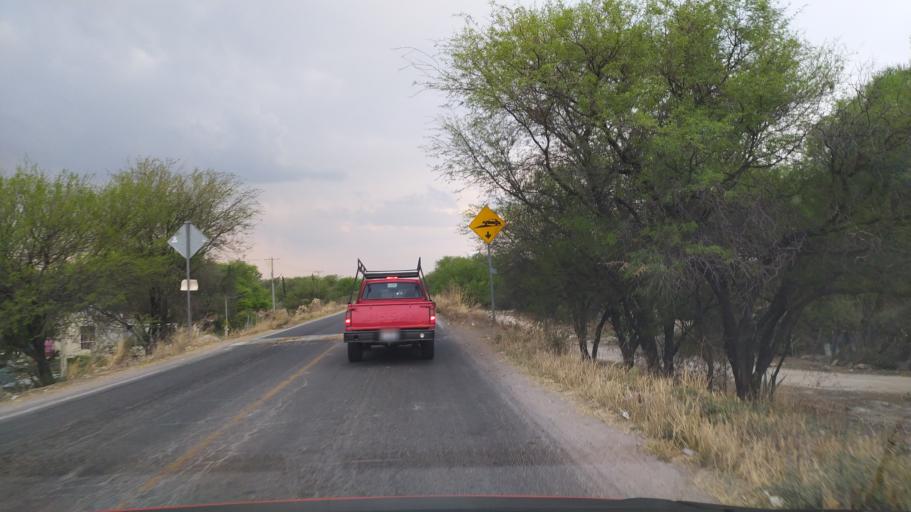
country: MX
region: Guanajuato
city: Ciudad Manuel Doblado
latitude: 20.8154
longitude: -101.9038
